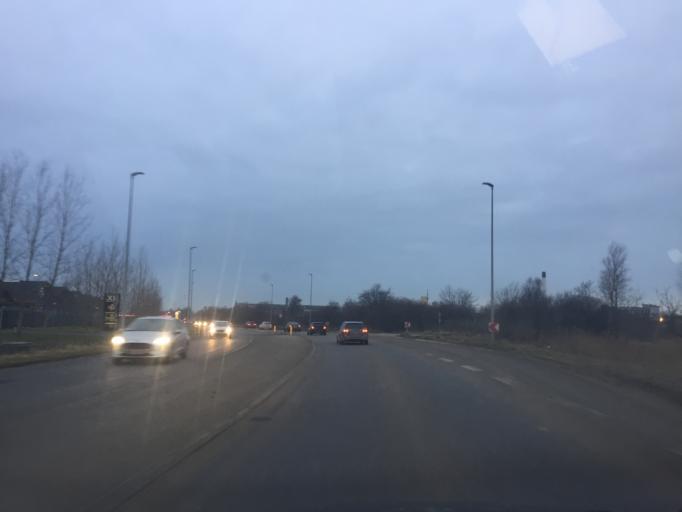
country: DK
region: Zealand
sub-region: Koge Kommune
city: Koge
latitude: 55.4792
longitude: 12.1931
